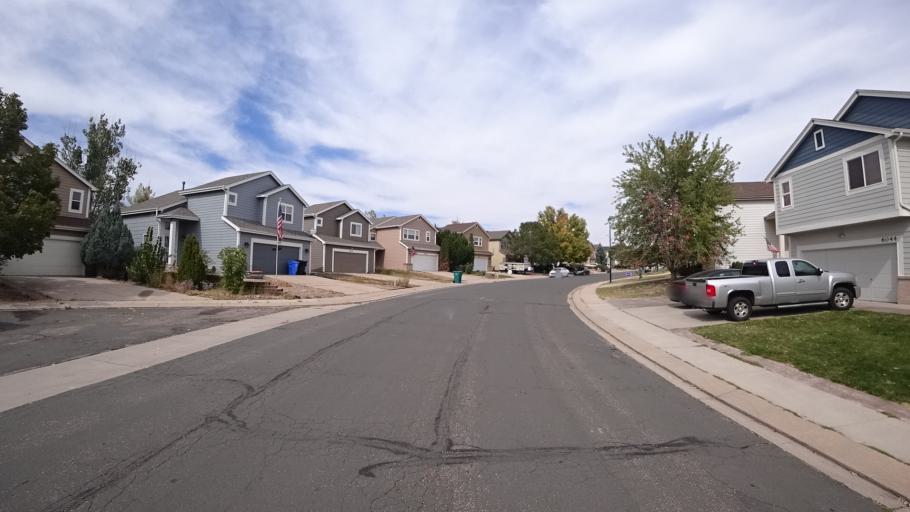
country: US
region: Colorado
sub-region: El Paso County
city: Cimarron Hills
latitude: 38.9070
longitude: -104.7073
